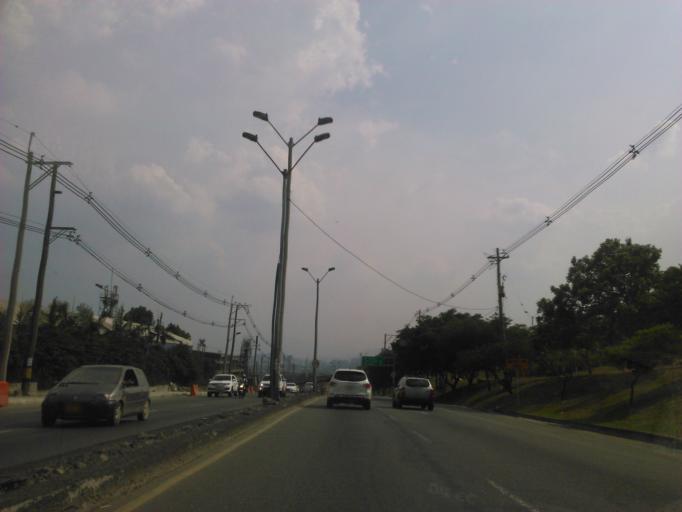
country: CO
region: Antioquia
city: Medellin
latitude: 6.2908
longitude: -75.5688
